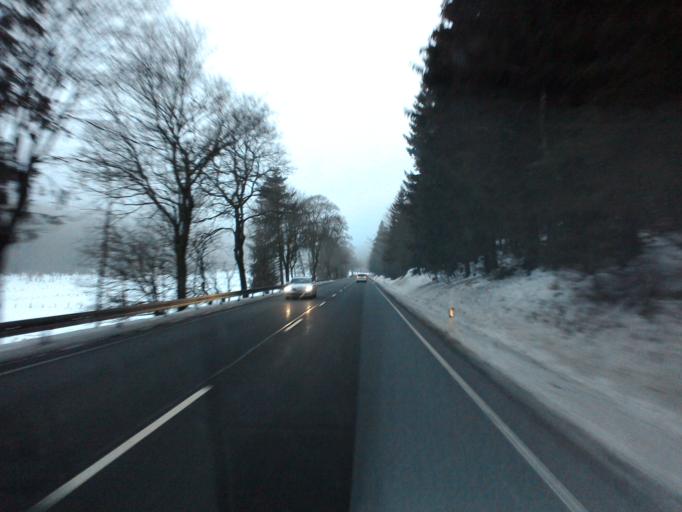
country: DE
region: North Rhine-Westphalia
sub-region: Regierungsbezirk Arnsberg
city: Winterberg
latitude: 51.2317
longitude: 8.5305
